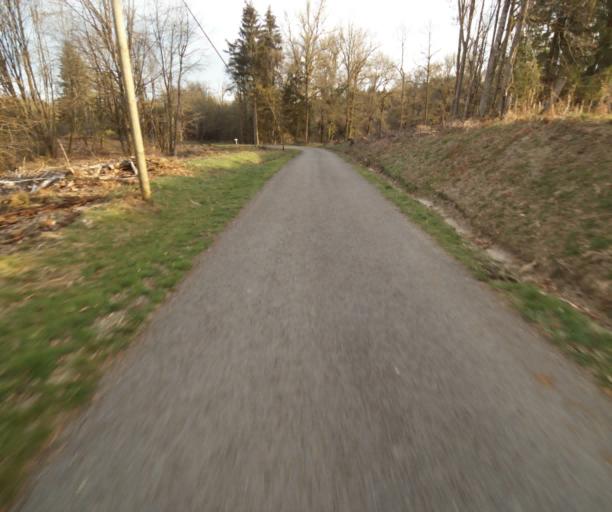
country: FR
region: Limousin
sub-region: Departement de la Correze
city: Argentat
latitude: 45.2258
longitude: 1.9702
